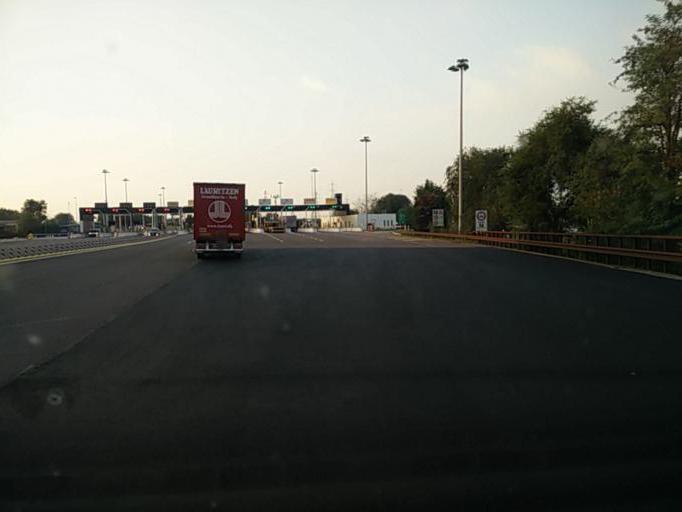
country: IT
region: Veneto
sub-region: Provincia di Verona
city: Caselle
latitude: 45.4320
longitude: 10.9104
